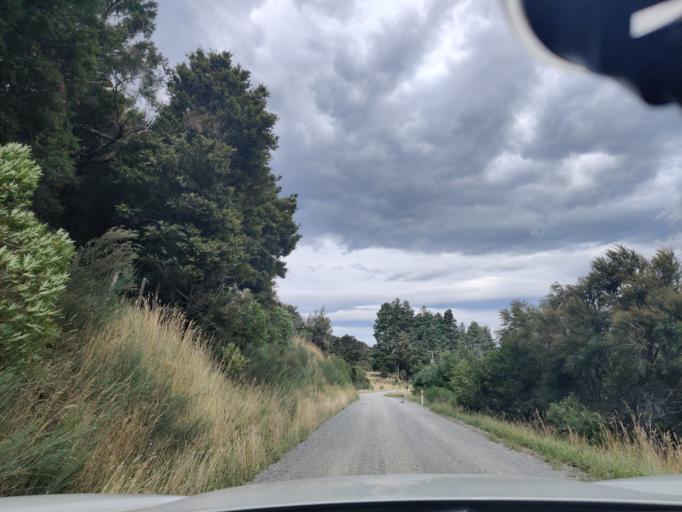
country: NZ
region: Wellington
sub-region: Masterton District
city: Masterton
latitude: -41.0346
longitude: 175.3990
